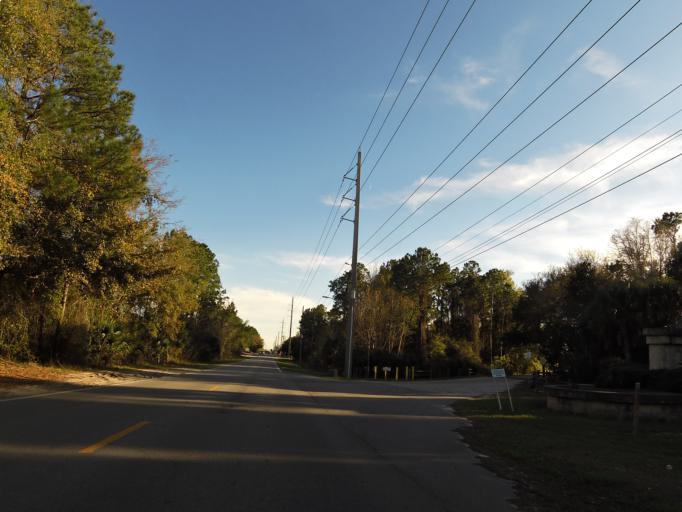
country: US
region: Florida
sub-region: Duval County
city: Jacksonville
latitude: 30.4308
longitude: -81.6030
